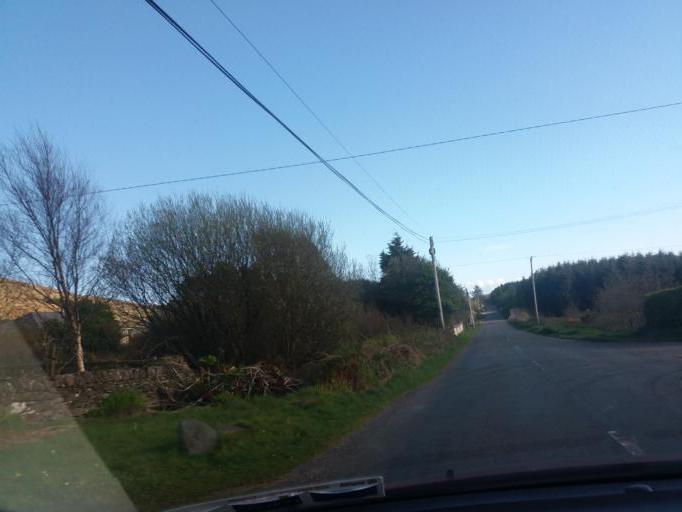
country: IE
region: Munster
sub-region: Ciarrai
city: Dingle
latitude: 52.1724
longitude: -10.2909
